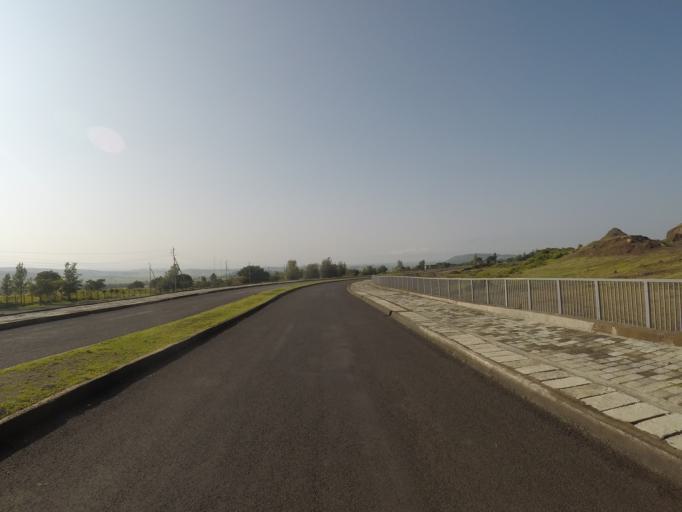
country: ET
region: Amhara
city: Gondar
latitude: 12.5267
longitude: 37.4302
